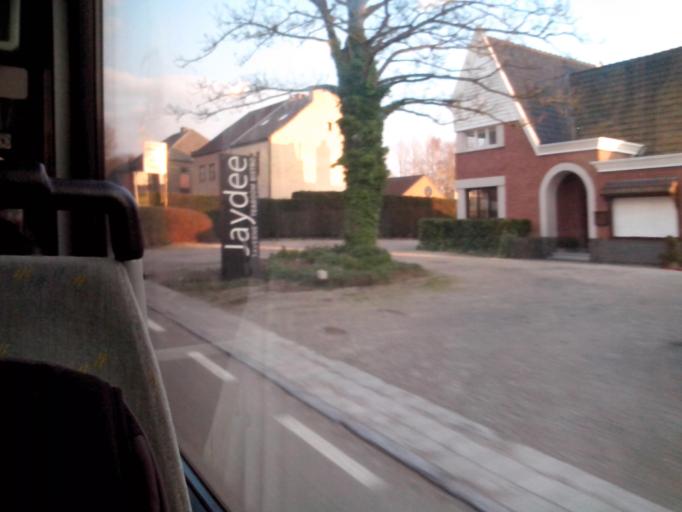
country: BE
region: Flanders
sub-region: Provincie Oost-Vlaanderen
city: Denderleeuw
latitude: 50.9155
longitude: 4.0850
